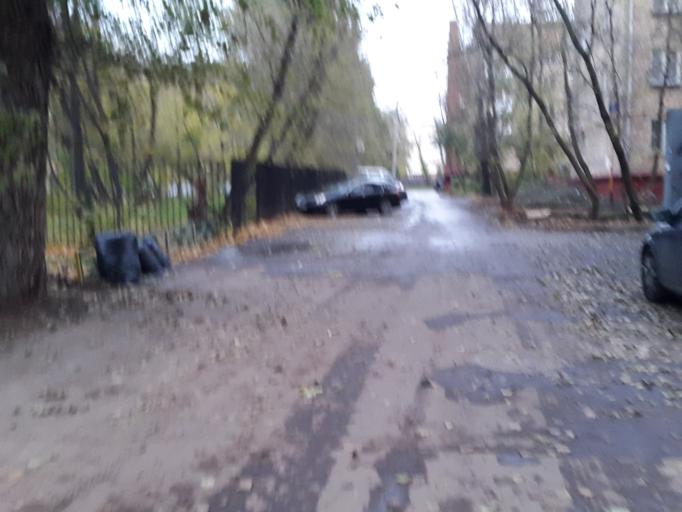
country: RU
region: Moscow
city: Pokrovskoye-Streshnevo
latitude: 55.8136
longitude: 37.4546
